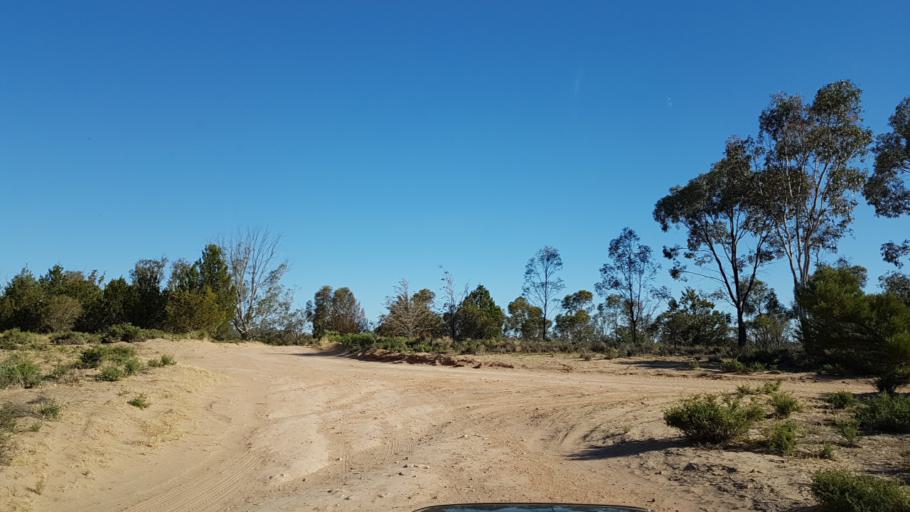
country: AU
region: South Australia
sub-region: Loxton Waikerie
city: Waikerie
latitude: -34.1549
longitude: 140.0214
